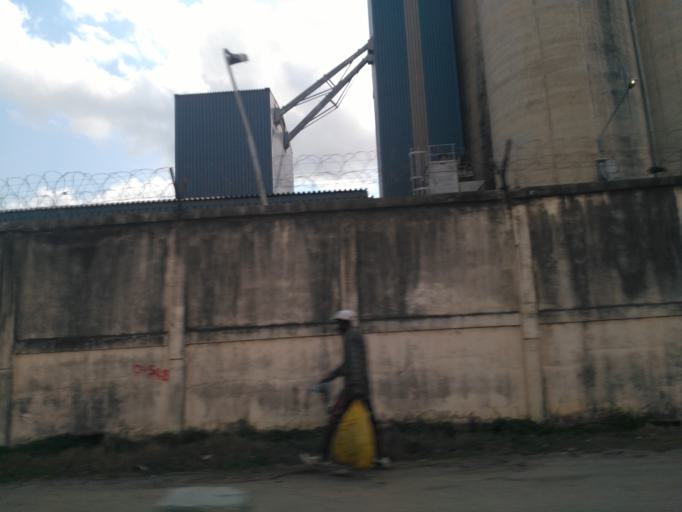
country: TZ
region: Dar es Salaam
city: Dar es Salaam
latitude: -6.8339
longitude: 39.2898
